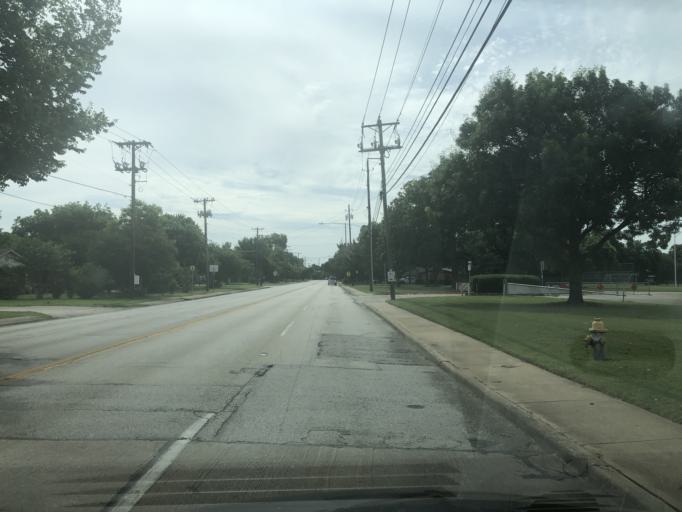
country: US
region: Texas
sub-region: Dallas County
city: Irving
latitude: 32.8017
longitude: -96.9845
